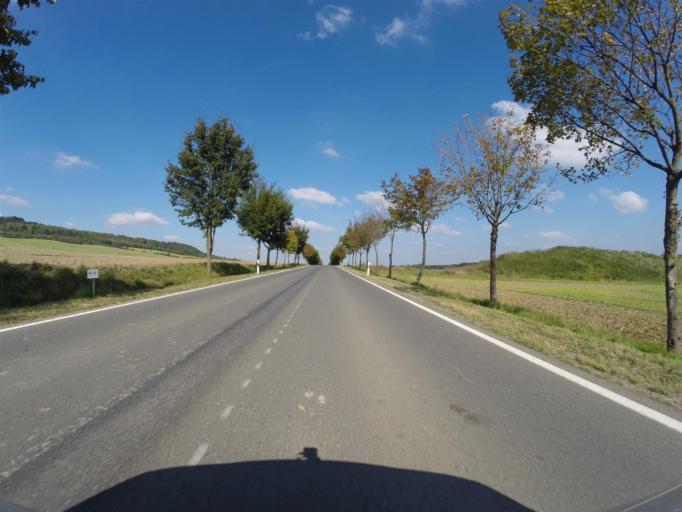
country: DE
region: Thuringia
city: Schongleina
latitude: 50.9008
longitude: 11.7099
